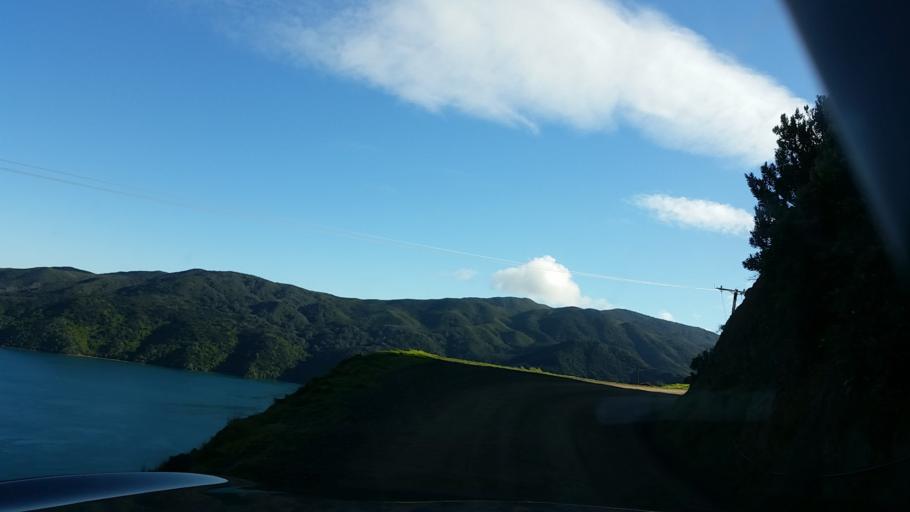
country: NZ
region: Marlborough
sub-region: Marlborough District
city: Picton
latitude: -40.9323
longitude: 173.8417
